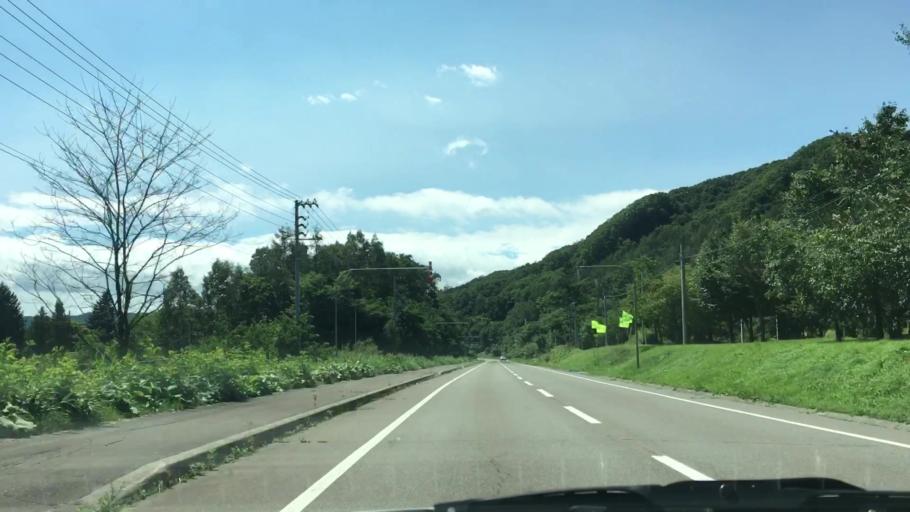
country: JP
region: Hokkaido
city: Otofuke
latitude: 43.2564
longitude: 143.5700
